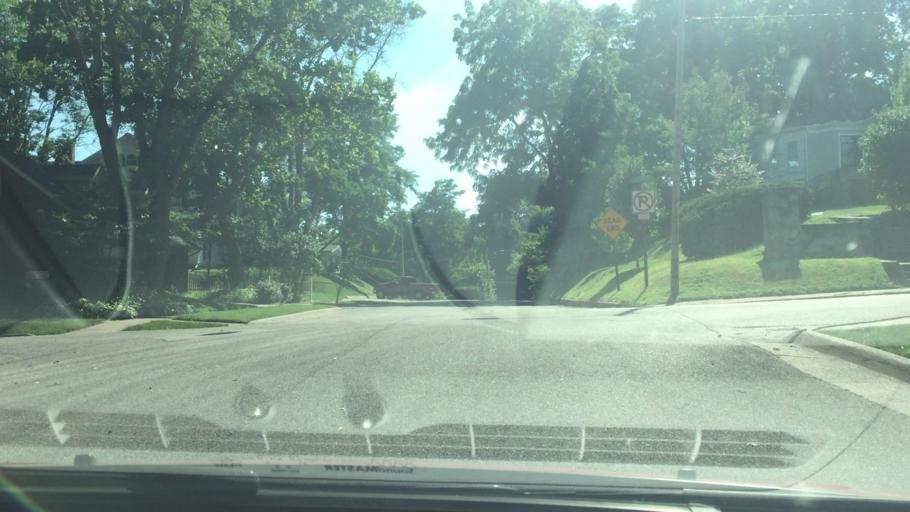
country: US
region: Iowa
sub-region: Muscatine County
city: Muscatine
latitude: 41.4184
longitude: -91.0509
